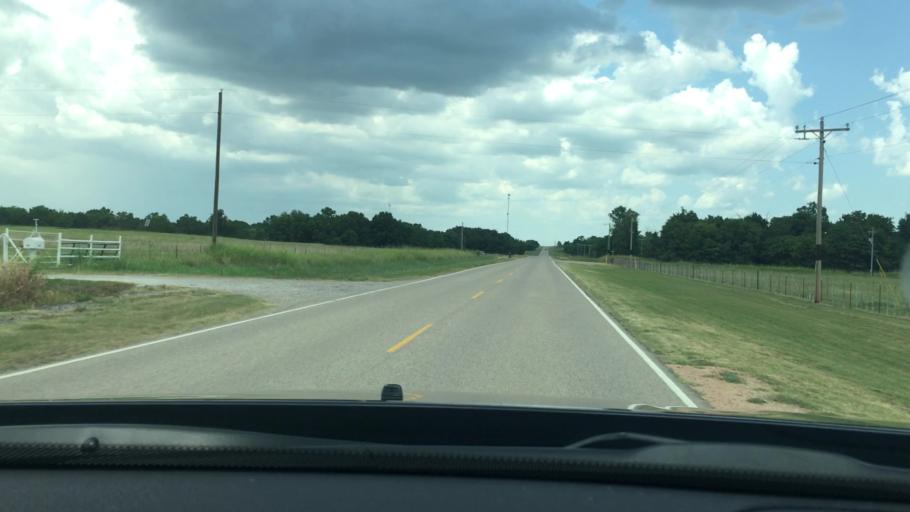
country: US
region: Oklahoma
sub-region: Johnston County
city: Tishomingo
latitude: 34.4176
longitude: -96.6359
